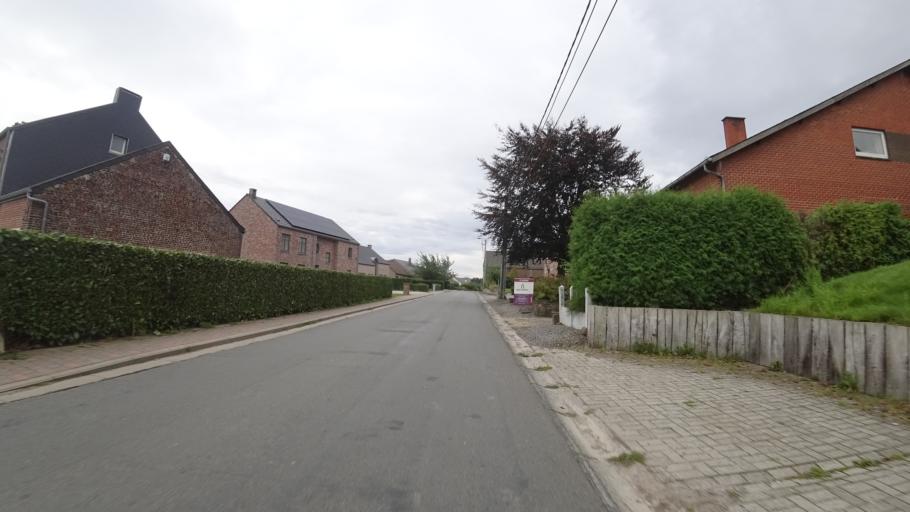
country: BE
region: Wallonia
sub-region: Province du Brabant Wallon
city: Perwez
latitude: 50.5561
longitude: 4.7975
